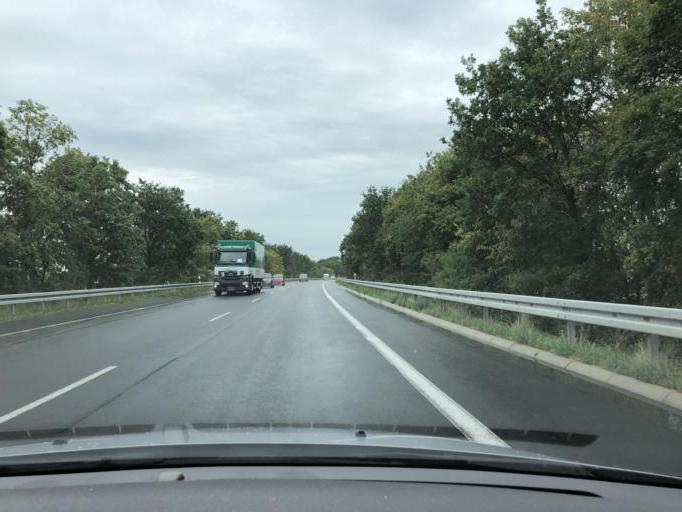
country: DE
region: North Rhine-Westphalia
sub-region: Regierungsbezirk Dusseldorf
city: Schermbeck
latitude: 51.6840
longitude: 6.8678
